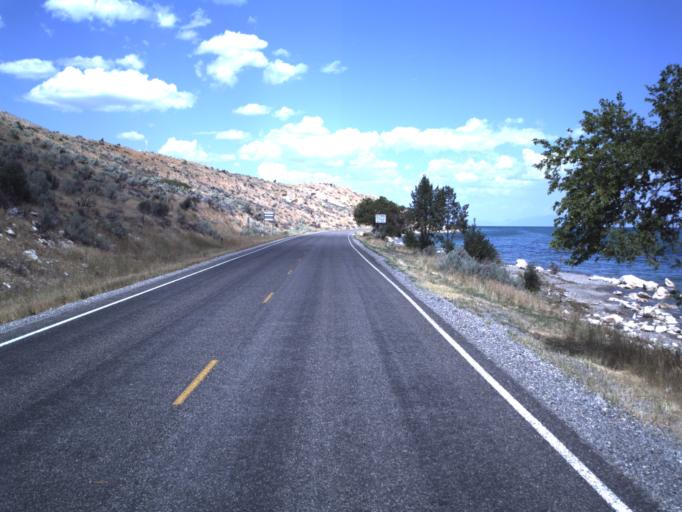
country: US
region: Utah
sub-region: Rich County
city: Randolph
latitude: 41.8686
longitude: -111.3651
